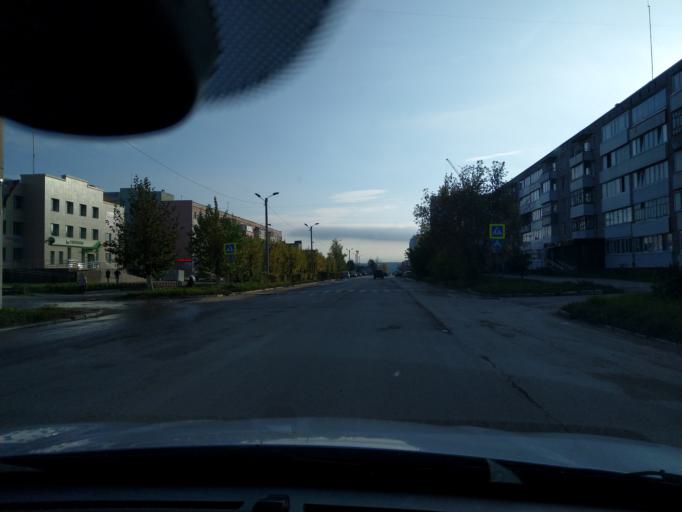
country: RU
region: Perm
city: Dobryanka
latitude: 58.4652
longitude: 56.4018
